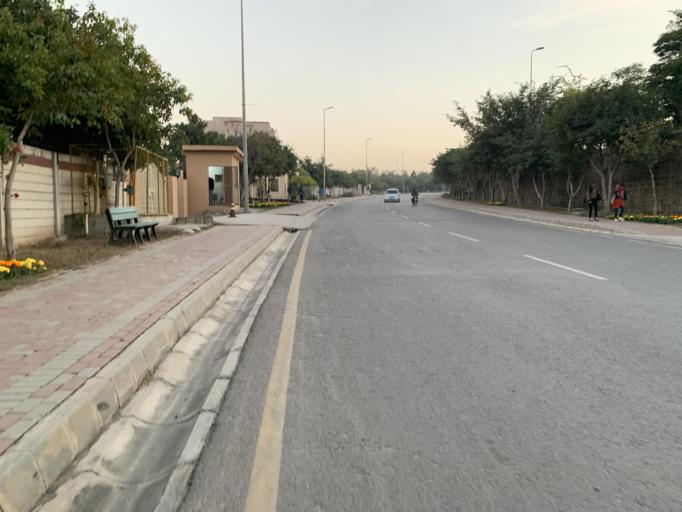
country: PK
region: Punjab
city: Rawalpindi
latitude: 33.6449
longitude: 72.9938
